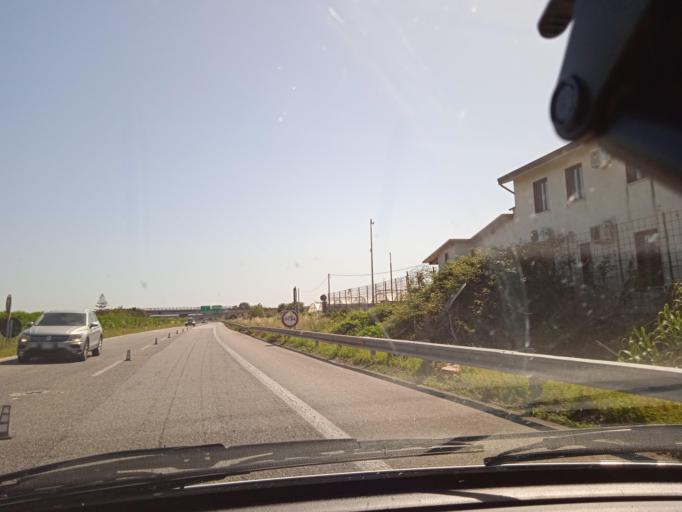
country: IT
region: Sicily
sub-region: Messina
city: Terme
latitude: 38.1529
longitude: 15.1818
